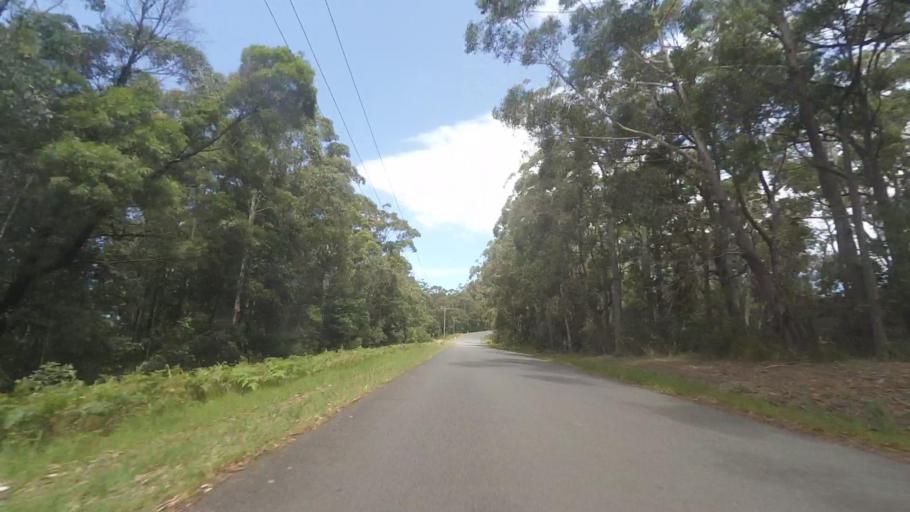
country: AU
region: New South Wales
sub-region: Shoalhaven Shire
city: Milton
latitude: -35.3911
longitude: 150.3676
